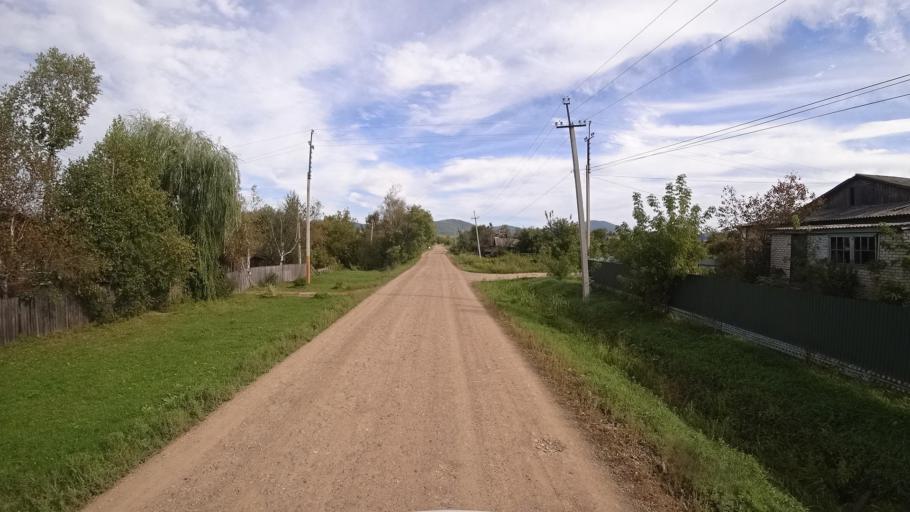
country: RU
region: Primorskiy
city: Dostoyevka
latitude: 44.3072
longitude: 133.4561
